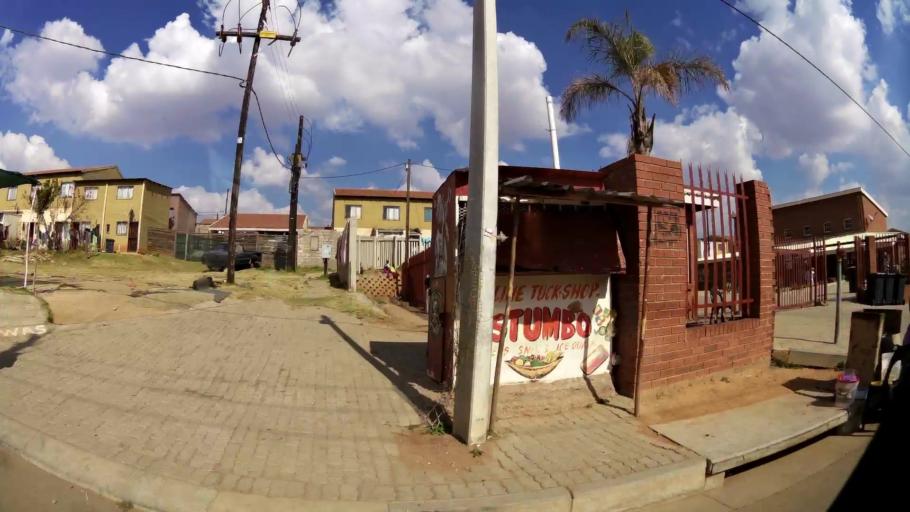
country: ZA
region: Gauteng
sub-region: City of Johannesburg Metropolitan Municipality
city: Roodepoort
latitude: -26.1839
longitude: 27.8445
